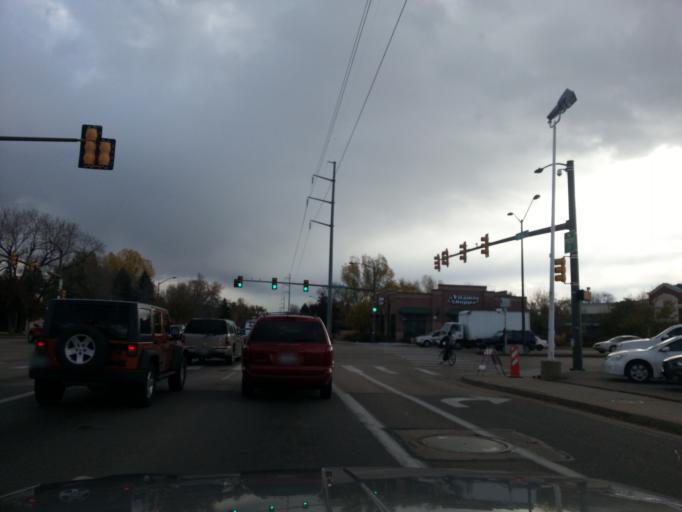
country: US
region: Colorado
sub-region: Larimer County
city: Fort Collins
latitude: 40.5525
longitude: -105.0776
